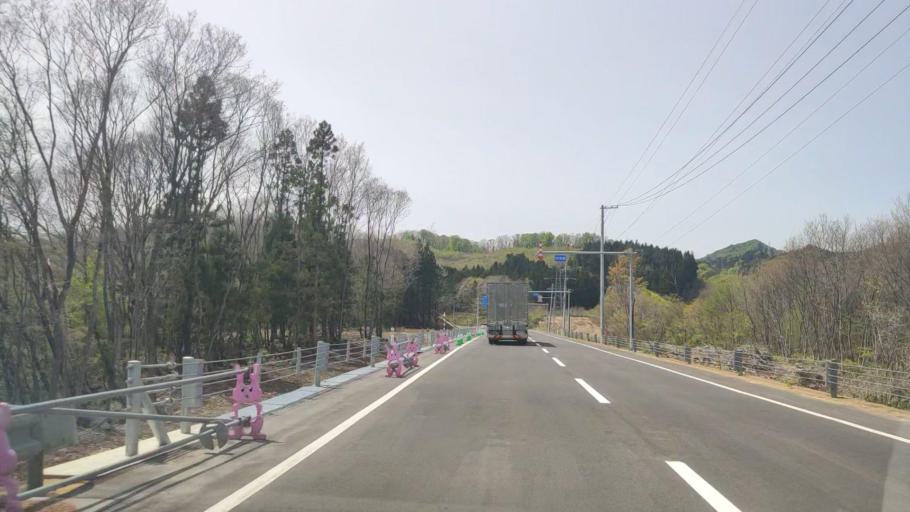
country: JP
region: Aomori
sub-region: Misawa Shi
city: Inuotose
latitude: 40.7874
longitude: 141.0758
